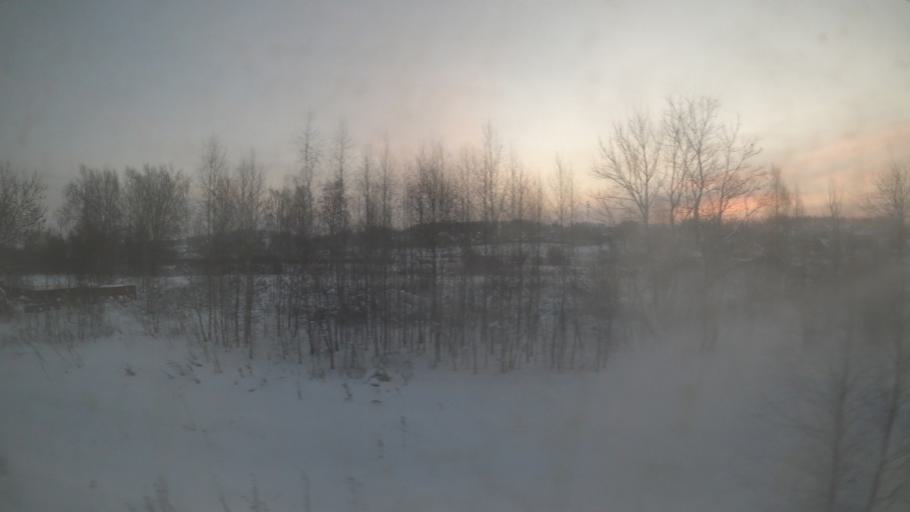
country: RU
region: Moskovskaya
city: Lugovaya
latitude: 56.0685
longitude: 37.4939
